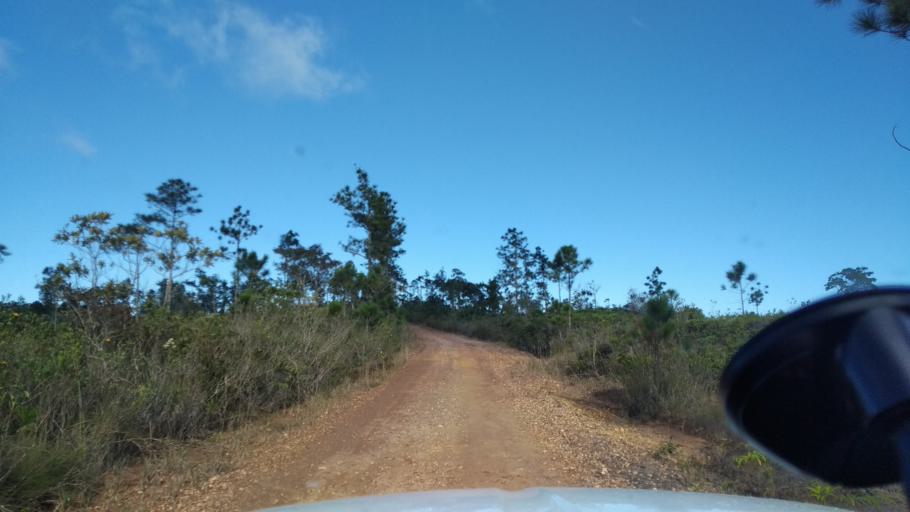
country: BZ
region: Cayo
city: Belmopan
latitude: 16.9965
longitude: -88.8376
